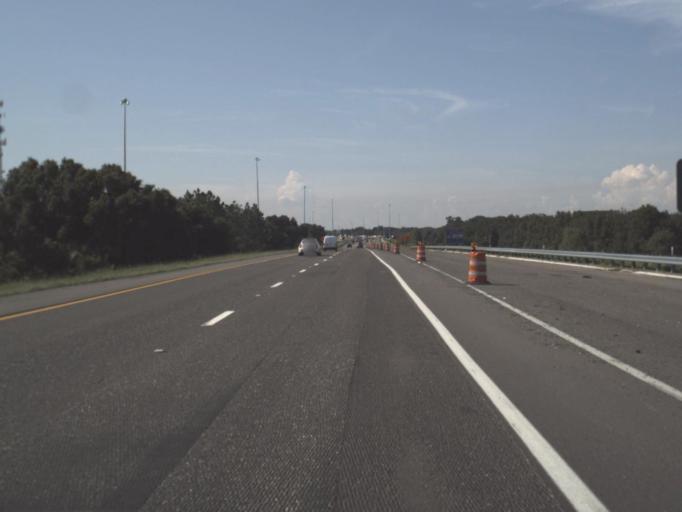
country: US
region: Florida
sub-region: Hillsborough County
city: Temple Terrace
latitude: 28.0693
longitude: -82.3541
